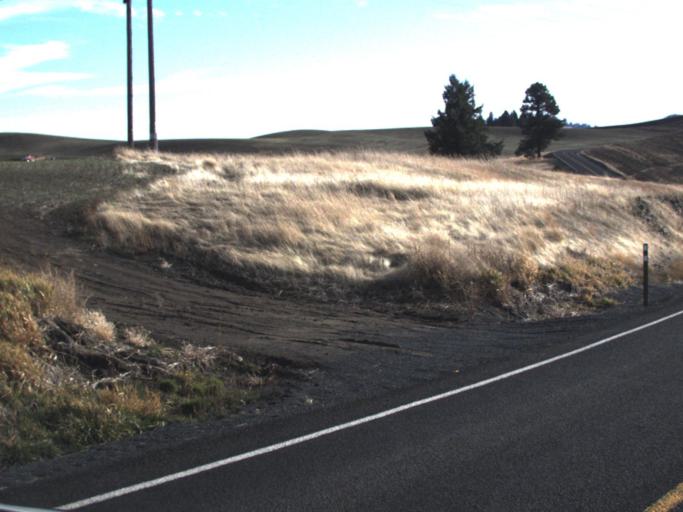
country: US
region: Washington
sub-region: Whitman County
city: Pullman
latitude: 46.9237
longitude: -117.1075
